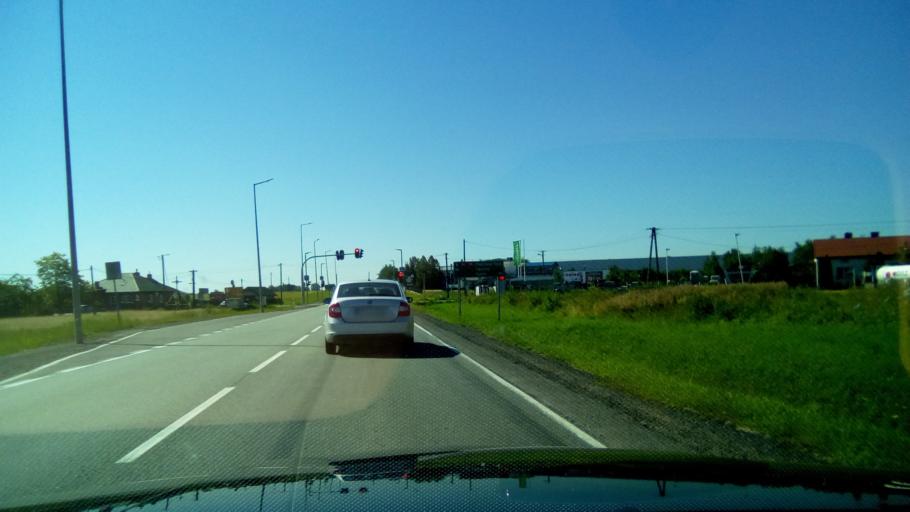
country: PL
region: Lodz Voivodeship
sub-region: Powiat piotrkowski
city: Moszczenica
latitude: 51.4642
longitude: 19.6626
